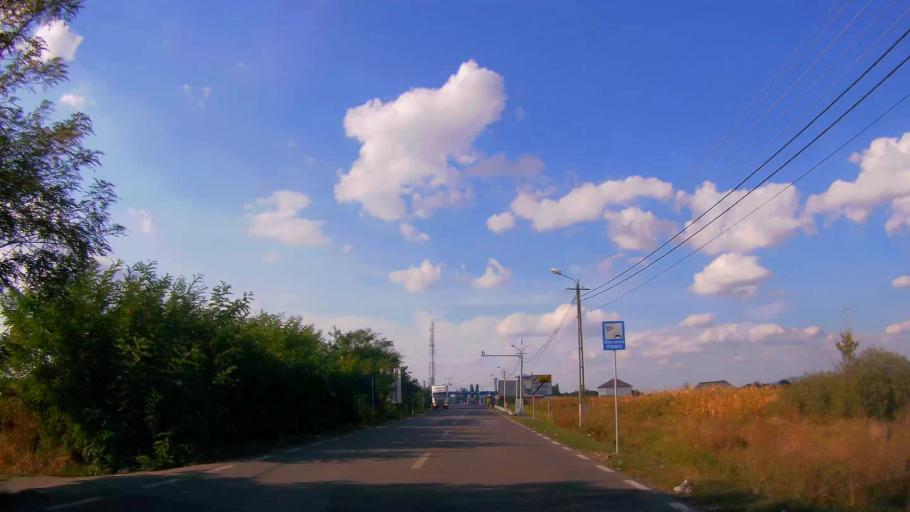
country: RO
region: Satu Mare
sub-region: Comuna Porumbesti
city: Porumbesti
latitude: 47.9898
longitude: 23.0046
